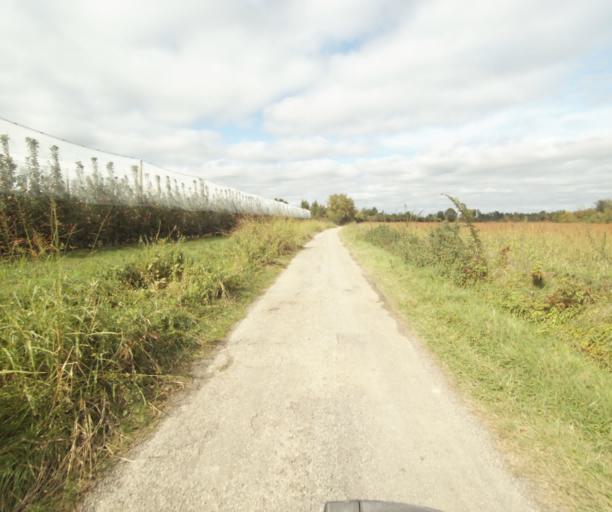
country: FR
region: Midi-Pyrenees
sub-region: Departement du Tarn-et-Garonne
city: Finhan
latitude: 43.9200
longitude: 1.2085
